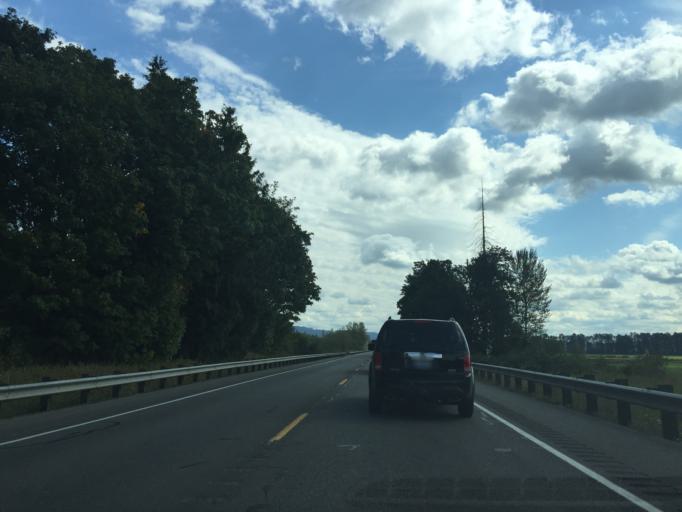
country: US
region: Washington
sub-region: Snohomish County
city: Three Lakes
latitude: 47.8927
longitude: -122.0300
